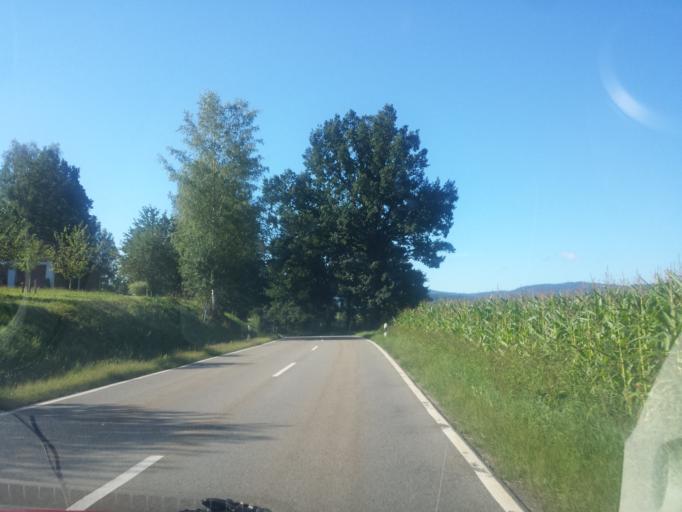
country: DE
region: Bavaria
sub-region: Lower Bavaria
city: Viechtach
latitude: 49.1019
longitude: 12.8865
